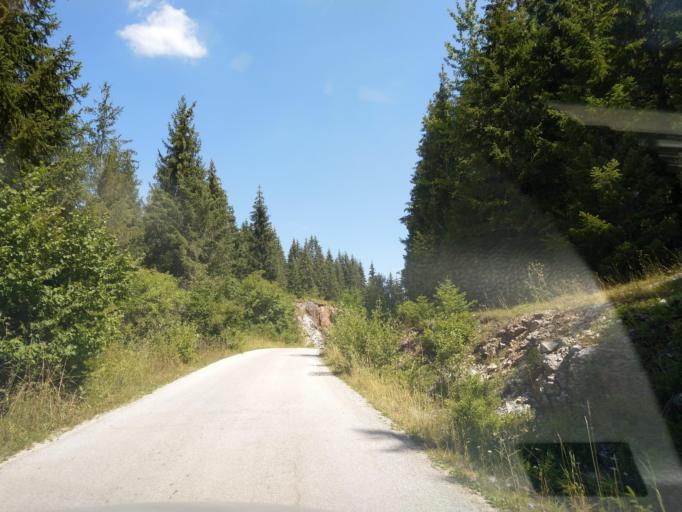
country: RS
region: Central Serbia
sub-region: Zlatiborski Okrug
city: Nova Varos
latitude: 43.4768
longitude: 19.9655
